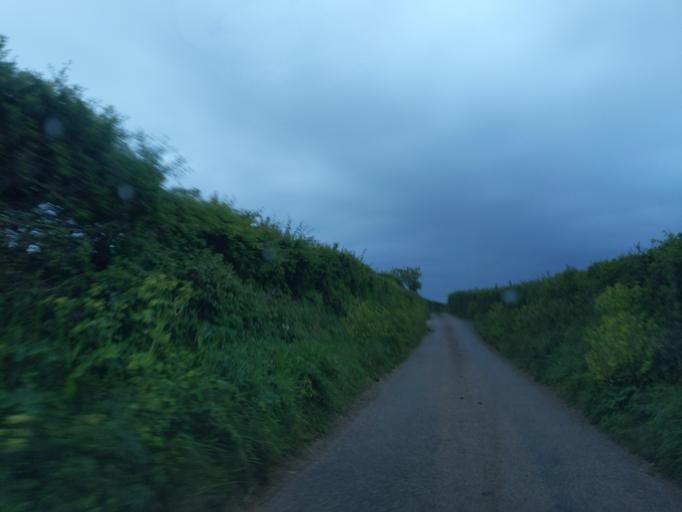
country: GB
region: England
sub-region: Borough of Torbay
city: Brixham
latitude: 50.3605
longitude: -3.5317
